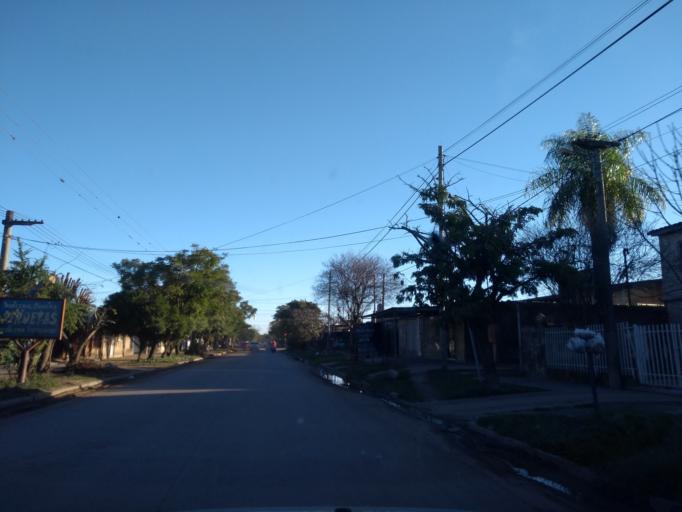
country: AR
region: Chaco
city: Puerto Vilelas
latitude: -27.4966
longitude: -58.9567
